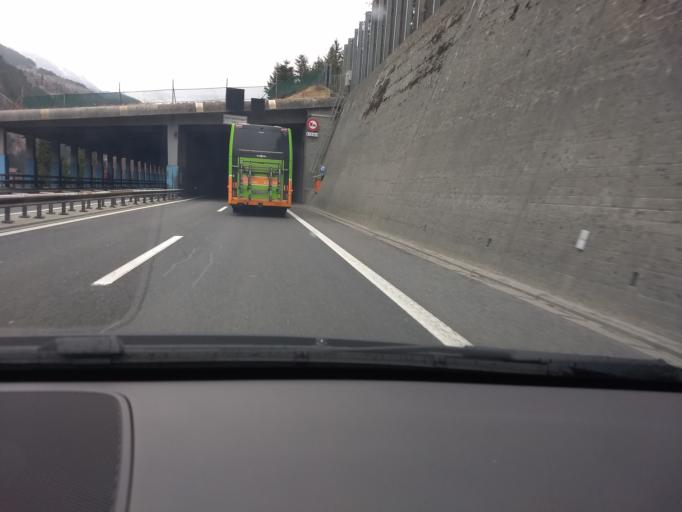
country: CH
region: Uri
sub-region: Uri
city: Silenen
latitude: 46.7207
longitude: 8.6181
